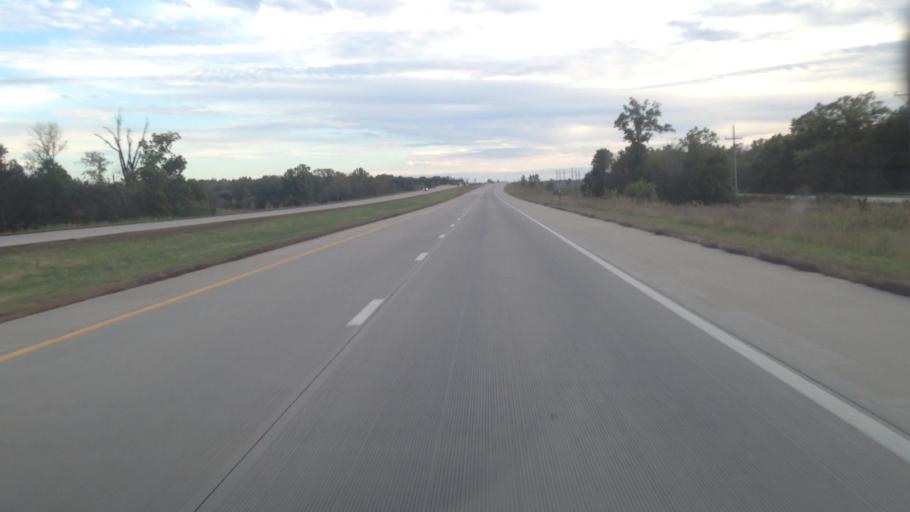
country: US
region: Kansas
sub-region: Douglas County
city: Baldwin City
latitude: 38.7458
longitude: -95.2677
